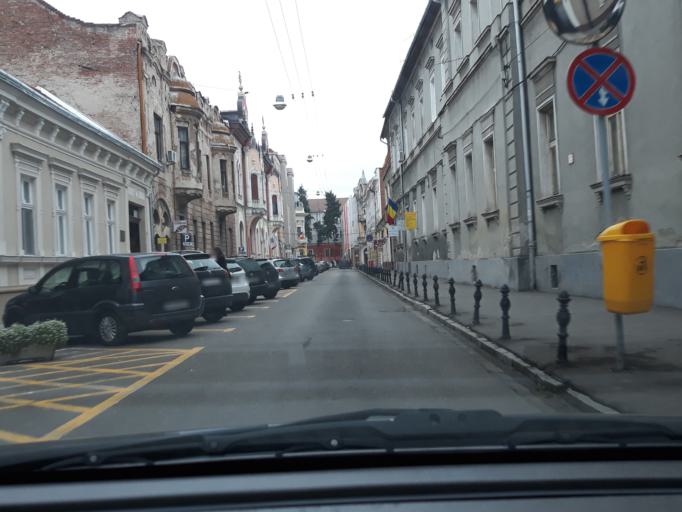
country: RO
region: Bihor
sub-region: Comuna Biharea
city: Oradea
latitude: 47.0593
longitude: 21.9325
